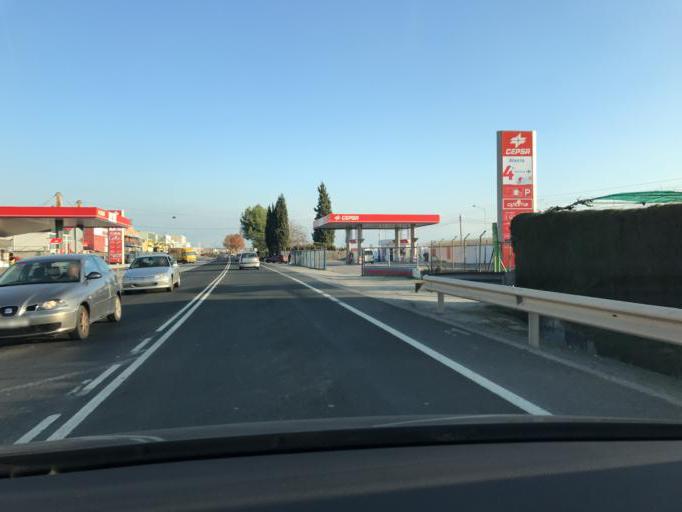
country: ES
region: Andalusia
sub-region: Provincia de Granada
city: Atarfe
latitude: 37.2127
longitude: -3.6855
